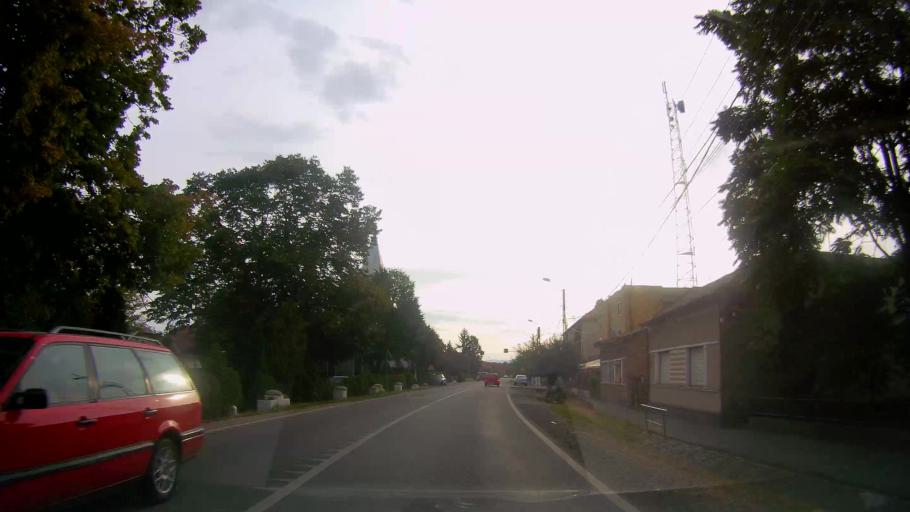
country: RO
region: Satu Mare
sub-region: Comuna Halmeu
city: Halmeu
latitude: 47.9769
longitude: 23.0189
